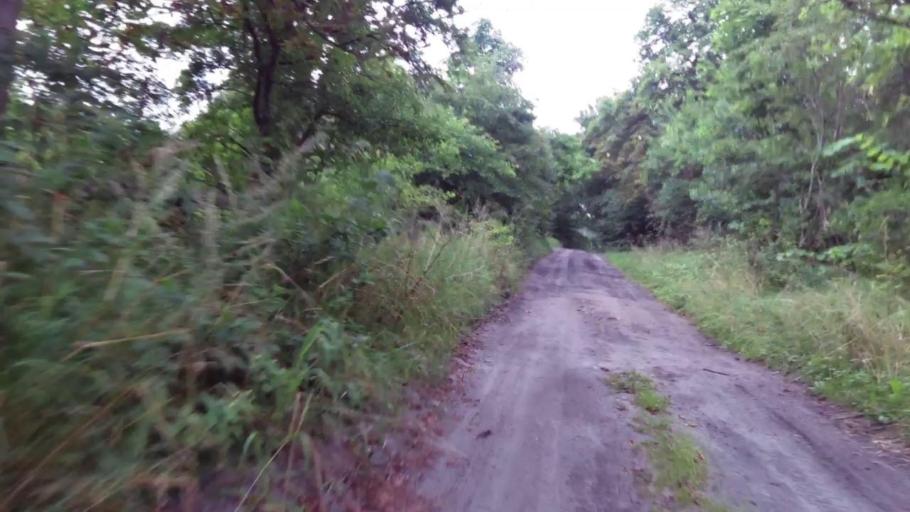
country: PL
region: West Pomeranian Voivodeship
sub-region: Powiat lobeski
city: Lobez
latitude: 53.5383
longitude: 15.6769
